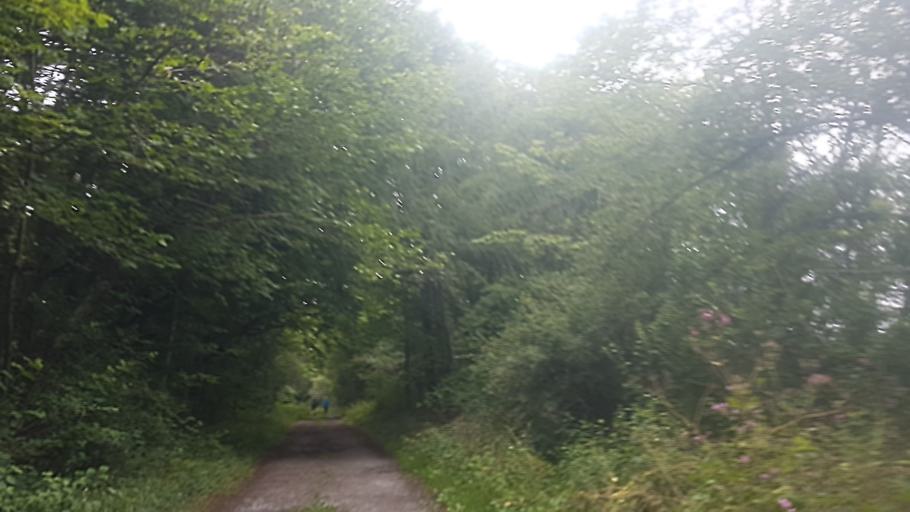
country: BE
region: Wallonia
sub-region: Province de Namur
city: Couvin
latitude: 50.0943
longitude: 4.5359
